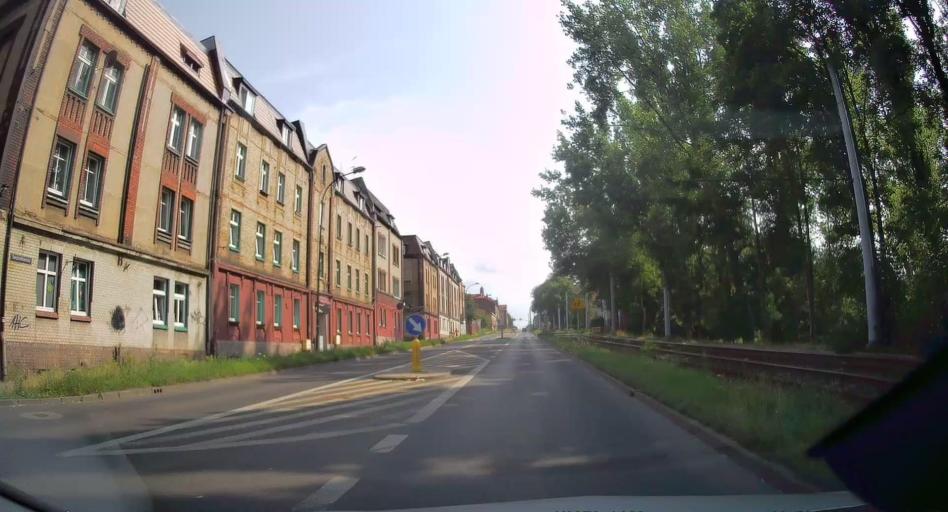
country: PL
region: Silesian Voivodeship
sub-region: Bytom
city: Bytom
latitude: 50.3269
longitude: 18.9279
